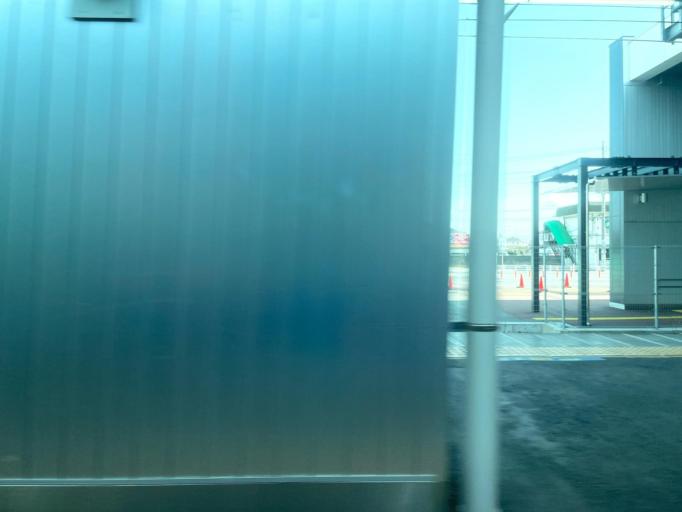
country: JP
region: Ibaraki
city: Ishioka
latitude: 36.1207
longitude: 140.2490
